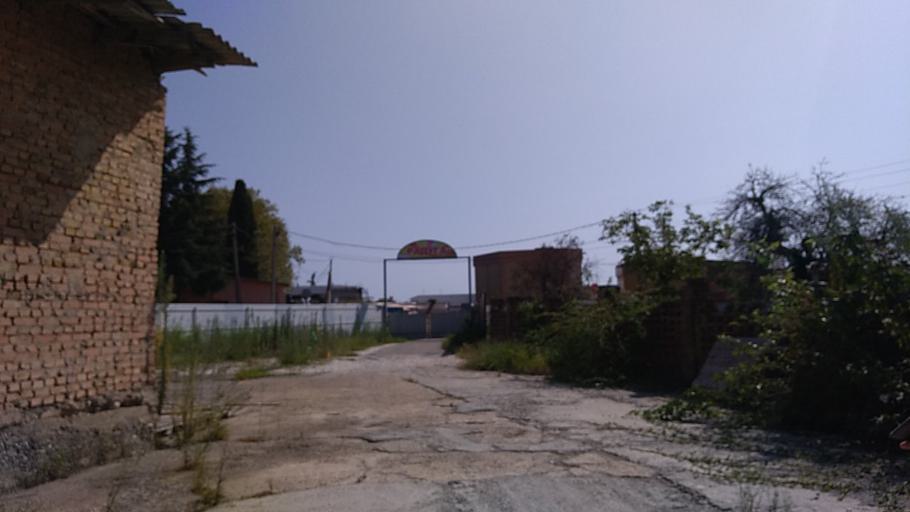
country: RU
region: Krasnodarskiy
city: Vysokoye
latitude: 43.4004
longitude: 39.9935
